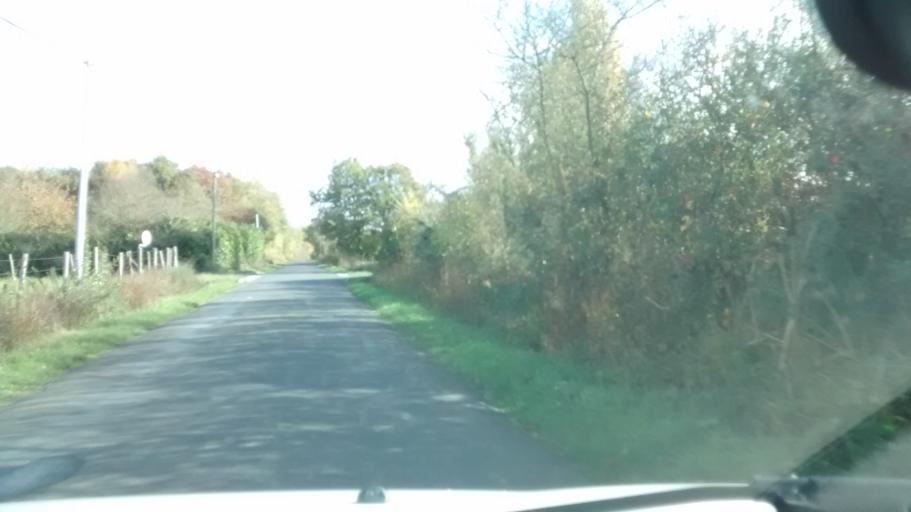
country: FR
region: Pays de la Loire
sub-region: Departement de Maine-et-Loire
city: Feneu
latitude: 47.5625
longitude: -0.5831
